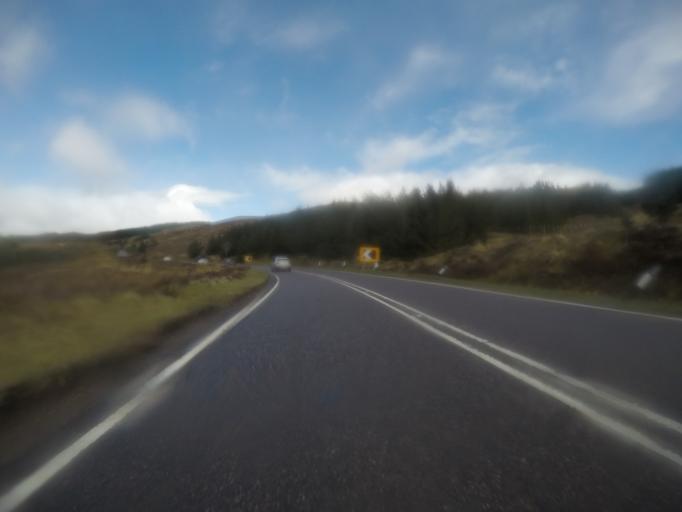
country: GB
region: Scotland
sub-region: Highland
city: Spean Bridge
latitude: 57.0859
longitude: -4.9619
